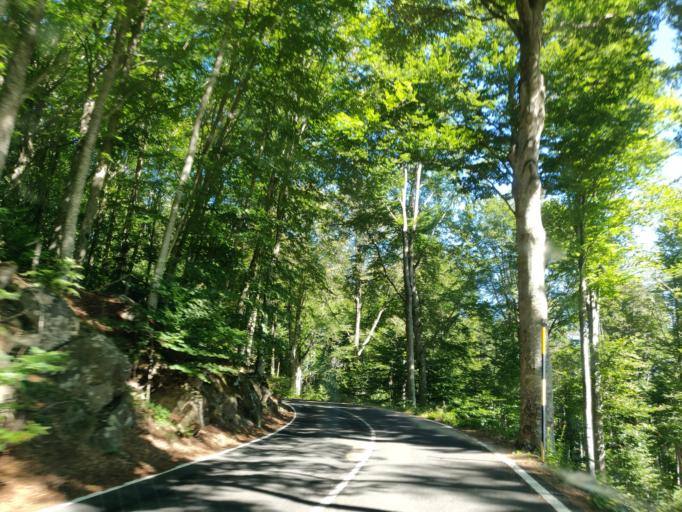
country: IT
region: Tuscany
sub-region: Provincia di Siena
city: Abbadia San Salvatore
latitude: 42.9015
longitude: 11.6384
